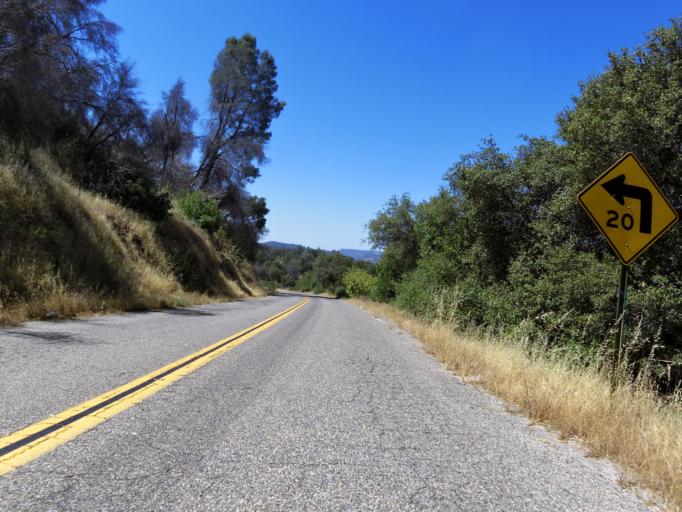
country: US
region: California
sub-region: Fresno County
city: Auberry
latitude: 37.1831
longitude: -119.5077
